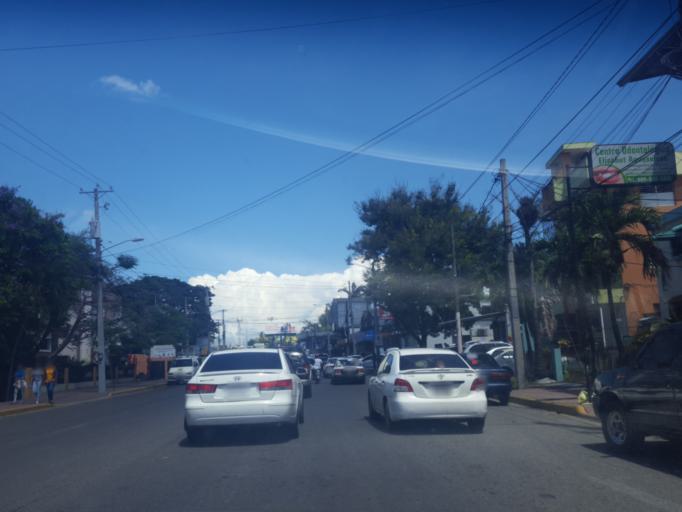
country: DO
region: Santiago
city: Santiago de los Caballeros
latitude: 19.4330
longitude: -70.6951
